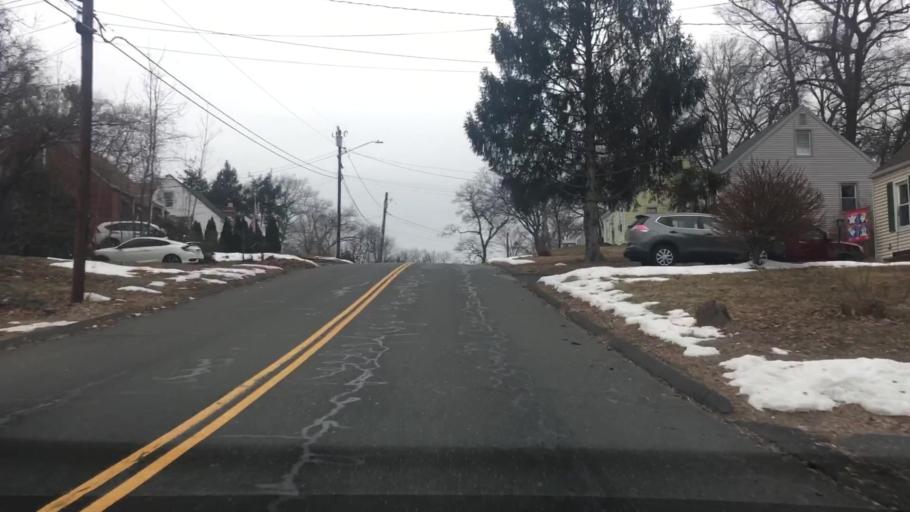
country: US
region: Connecticut
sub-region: Hartford County
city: Bristol
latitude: 41.6810
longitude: -72.9156
